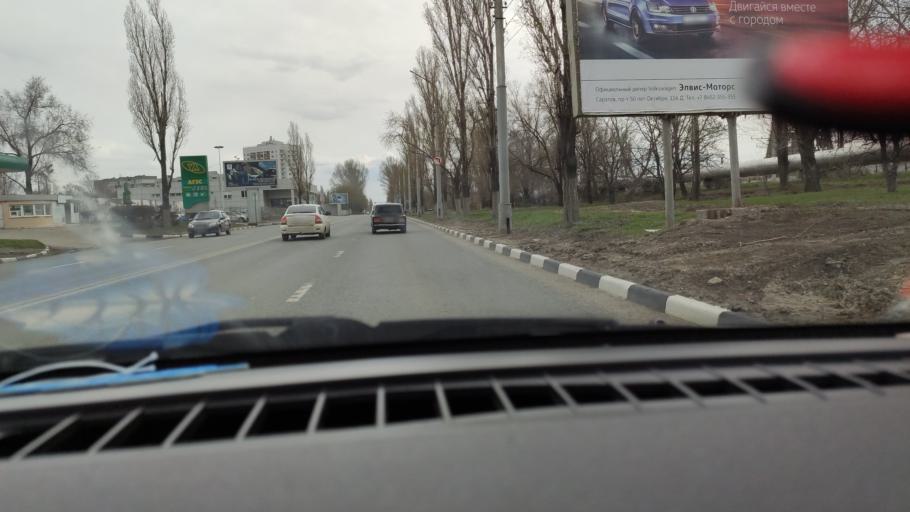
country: RU
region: Saratov
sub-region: Saratovskiy Rayon
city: Saratov
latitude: 51.5728
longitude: 45.9920
